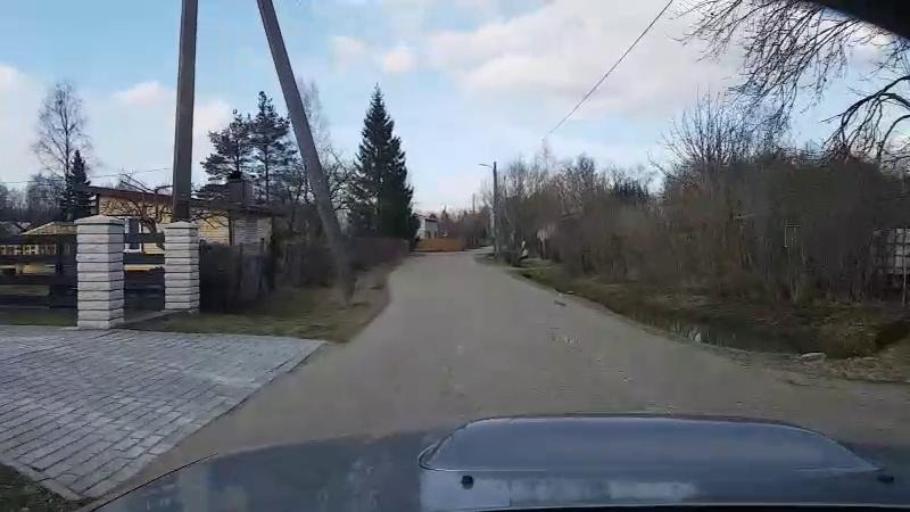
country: EE
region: Jaervamaa
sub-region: Paide linn
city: Paide
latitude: 58.8867
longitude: 25.5291
